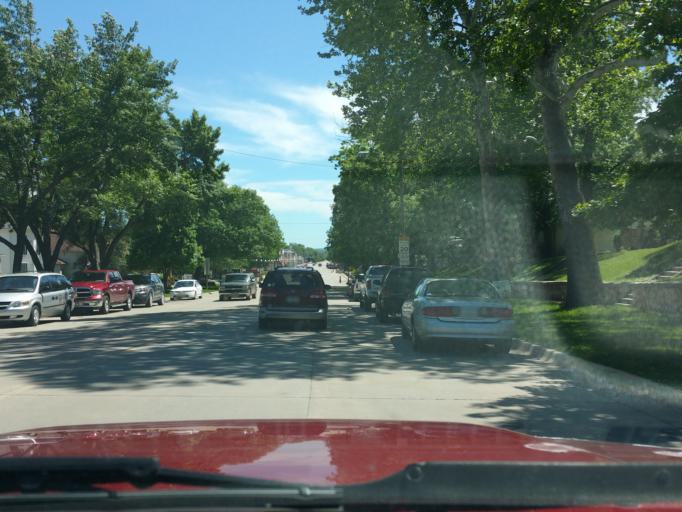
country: US
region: Kansas
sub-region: Pottawatomie County
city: Wamego
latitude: 39.2059
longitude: -96.3051
